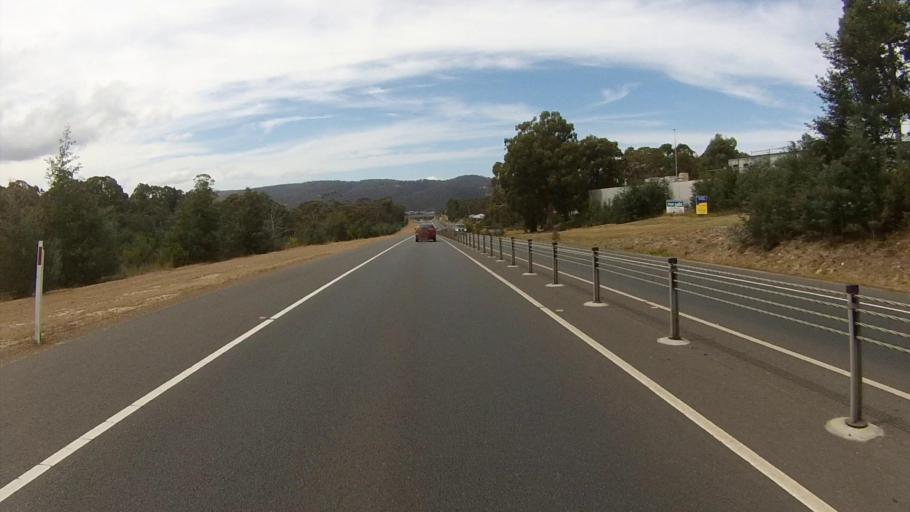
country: AU
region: Tasmania
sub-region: Kingborough
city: Kingston
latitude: -42.9807
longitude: 147.2930
